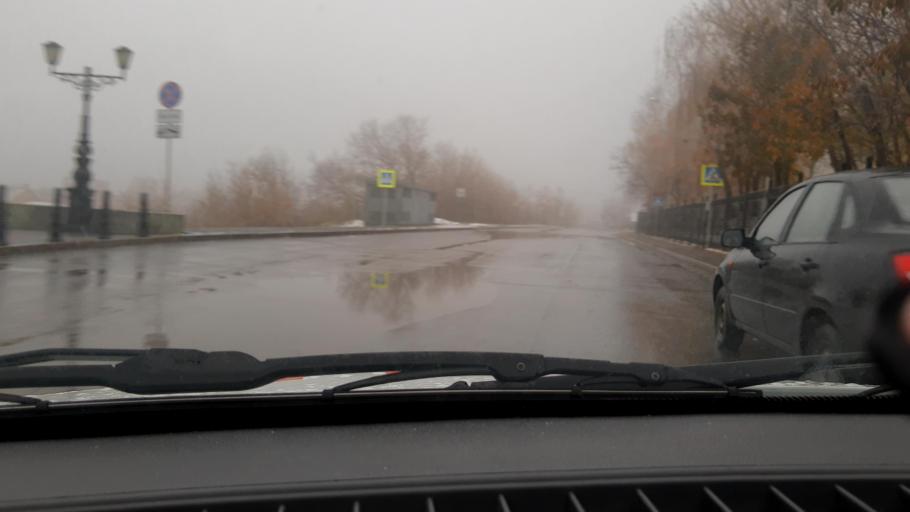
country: RU
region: Bashkortostan
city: Ufa
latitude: 54.7208
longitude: 55.9255
